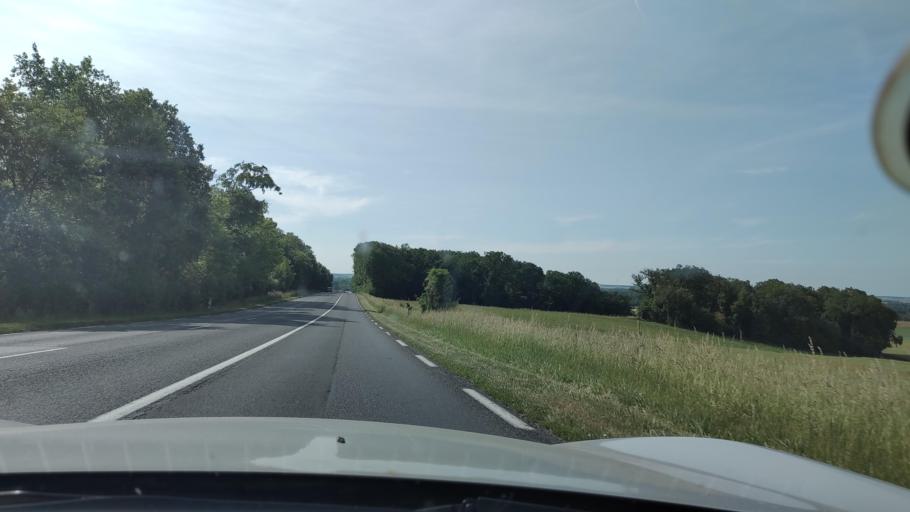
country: FR
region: Ile-de-France
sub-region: Departement de Seine-et-Marne
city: Sourdun
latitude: 48.5212
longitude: 3.4149
